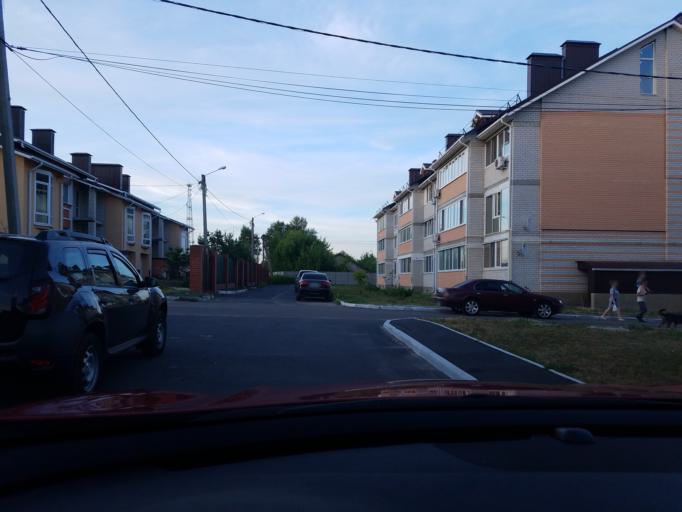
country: RU
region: Orjol
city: Znamenka
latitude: 52.9108
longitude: 36.0081
